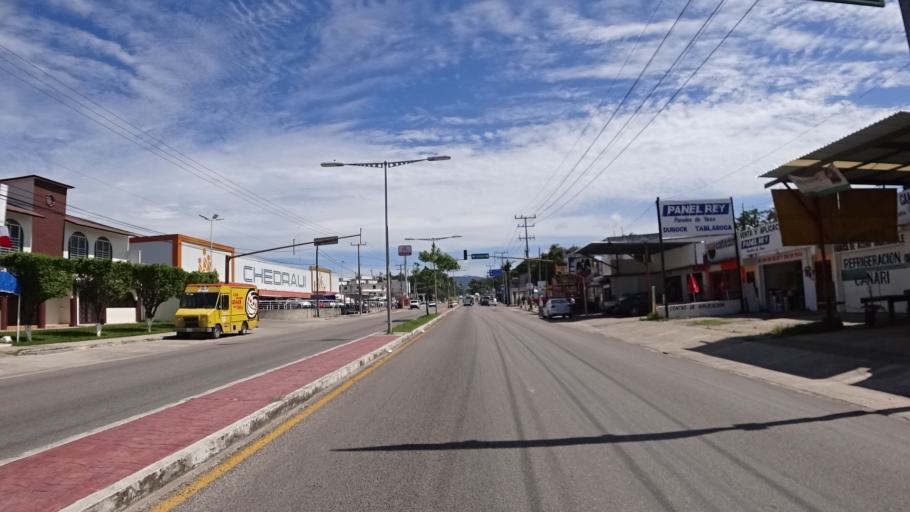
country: MX
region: Chiapas
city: Palenque
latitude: 17.5133
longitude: -91.9920
